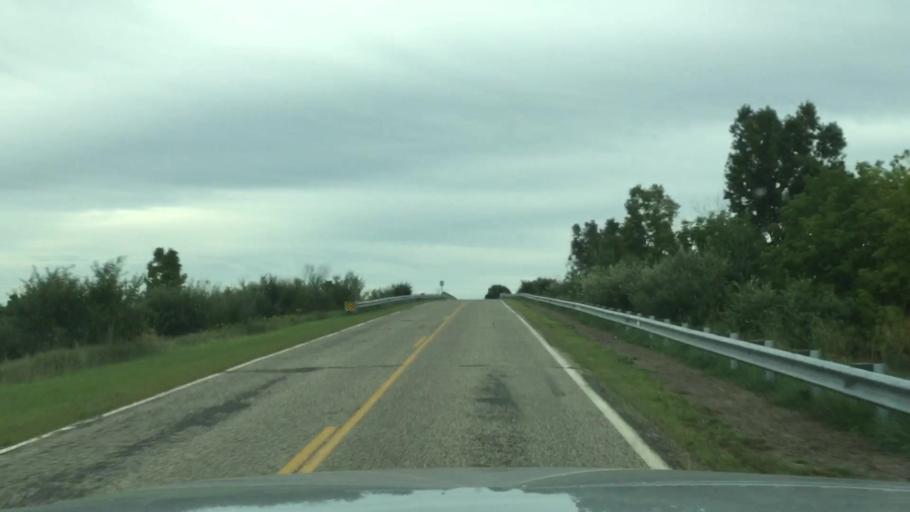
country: US
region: Michigan
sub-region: Shiawassee County
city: Durand
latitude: 42.9048
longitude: -84.0694
